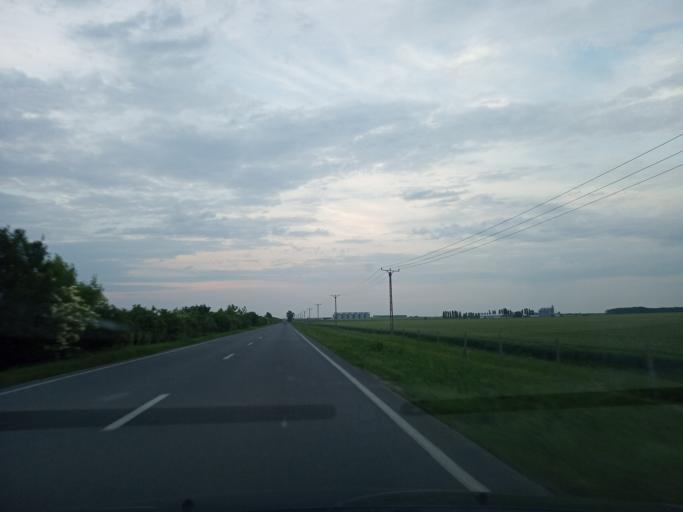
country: RO
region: Timis
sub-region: Oras Deta
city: Deta
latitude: 45.4288
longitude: 21.2305
